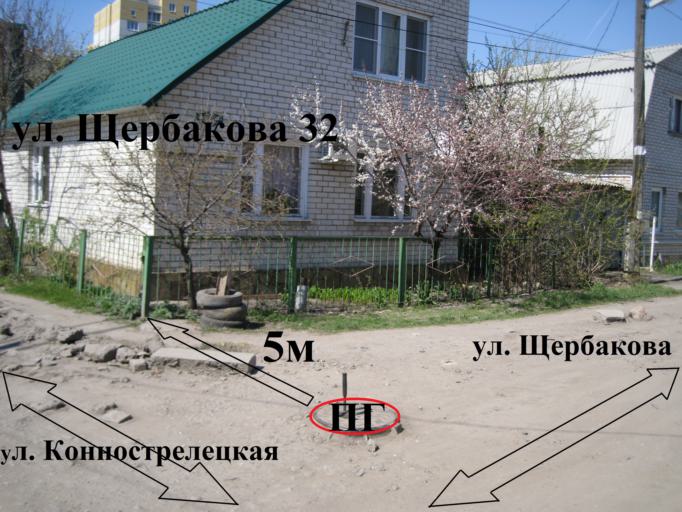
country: RU
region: Voronezj
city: Voronezh
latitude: 51.6496
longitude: 39.1818
